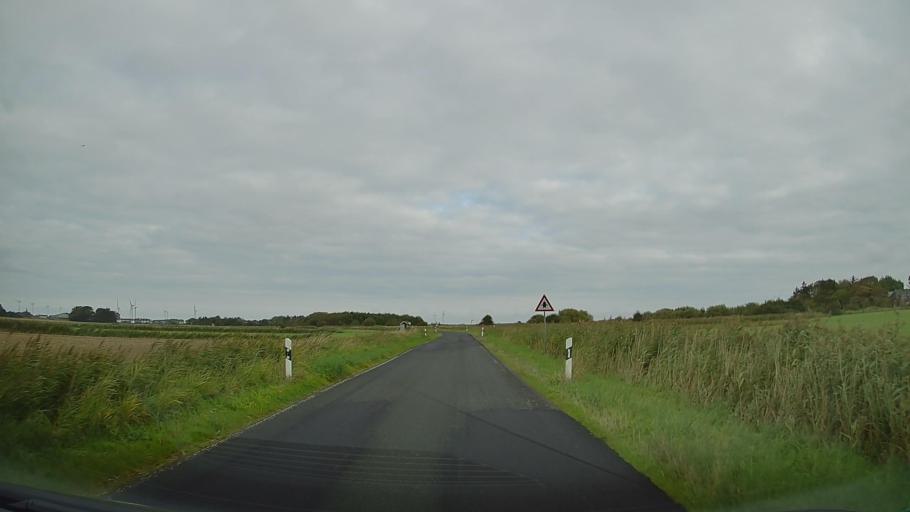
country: DE
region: Schleswig-Holstein
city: Emmelsbull-Horsbull
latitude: 54.8224
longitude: 8.6536
